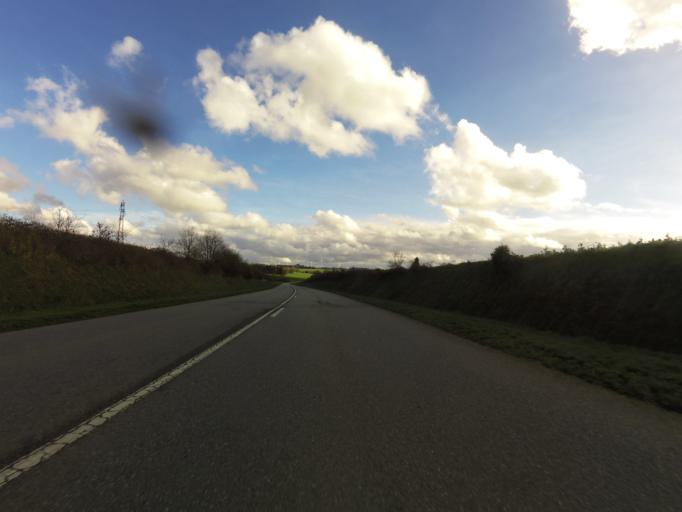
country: FR
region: Brittany
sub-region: Departement du Morbihan
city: Credin
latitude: 48.0175
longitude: -2.7990
